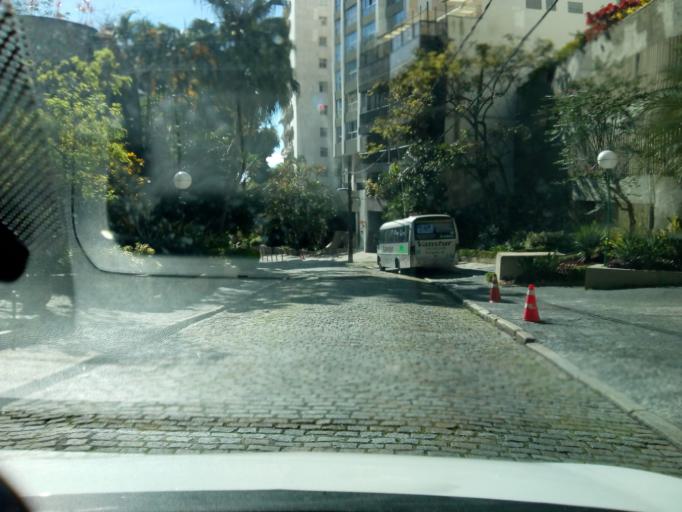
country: BR
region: Rio de Janeiro
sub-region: Rio De Janeiro
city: Rio de Janeiro
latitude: -22.9860
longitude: -43.2345
